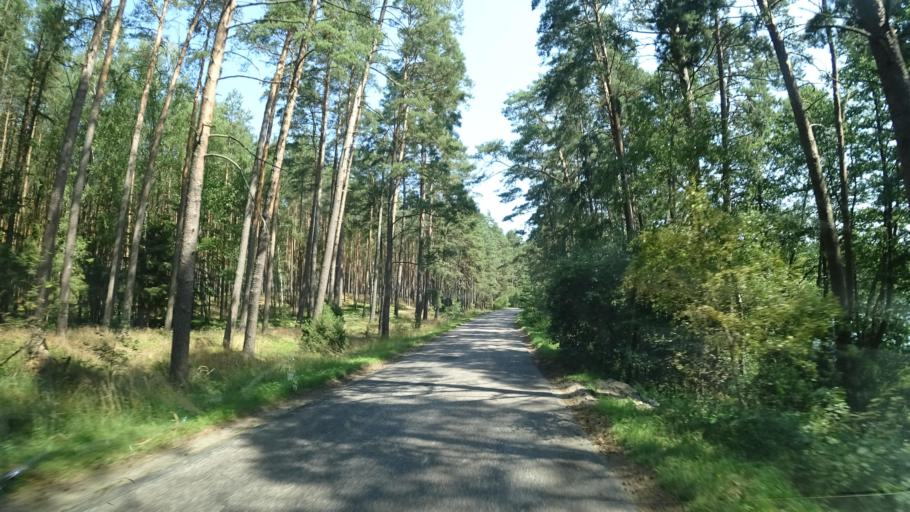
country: PL
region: Pomeranian Voivodeship
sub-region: Powiat chojnicki
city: Brusy
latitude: 53.8541
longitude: 17.5788
